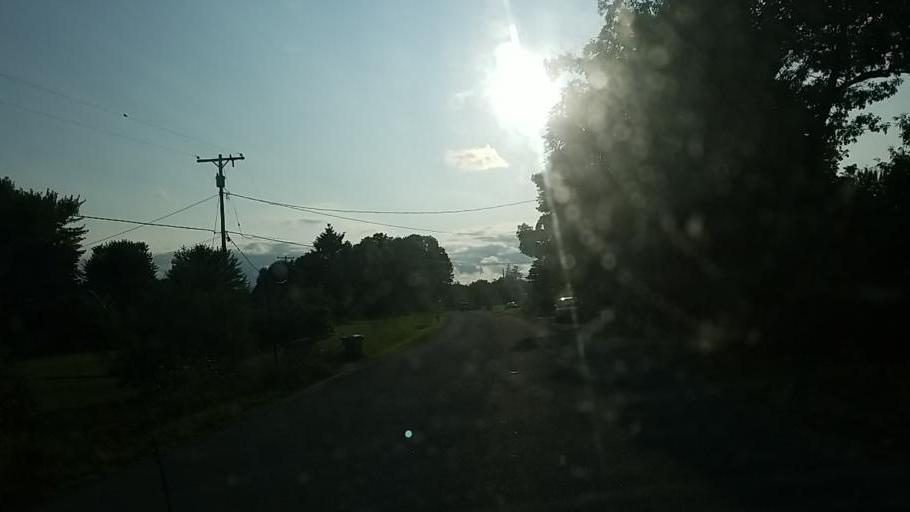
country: US
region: Michigan
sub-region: Montcalm County
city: Greenville
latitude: 43.2353
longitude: -85.3647
